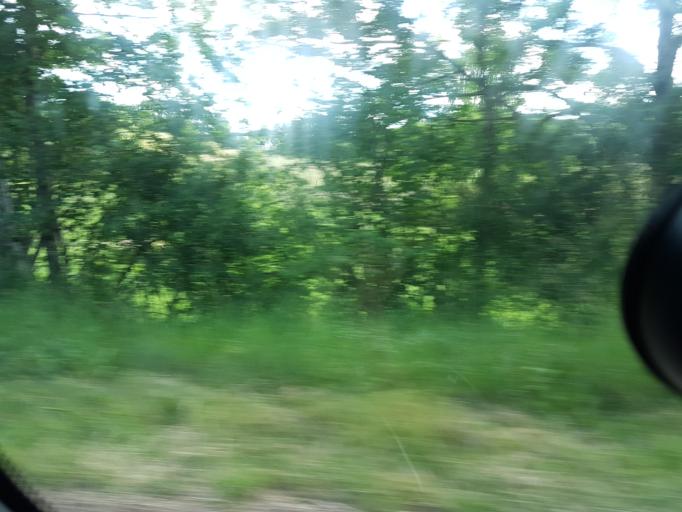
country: FR
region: Bourgogne
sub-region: Departement de la Cote-d'Or
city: Saulieu
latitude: 47.1691
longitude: 4.1547
